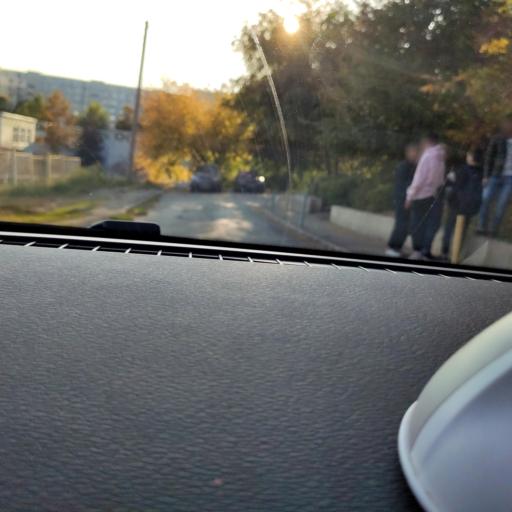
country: RU
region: Samara
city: Samara
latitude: 53.1921
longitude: 50.1464
